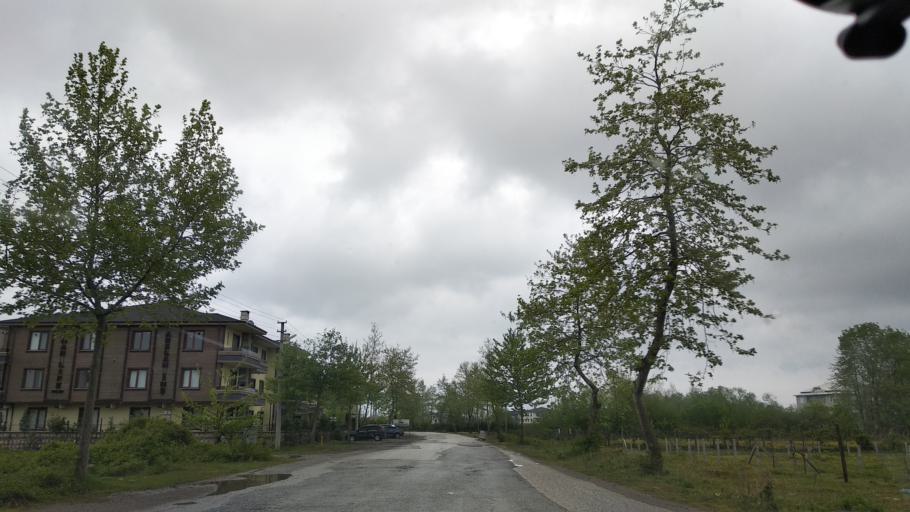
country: TR
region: Sakarya
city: Karasu
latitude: 41.0922
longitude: 30.7070
